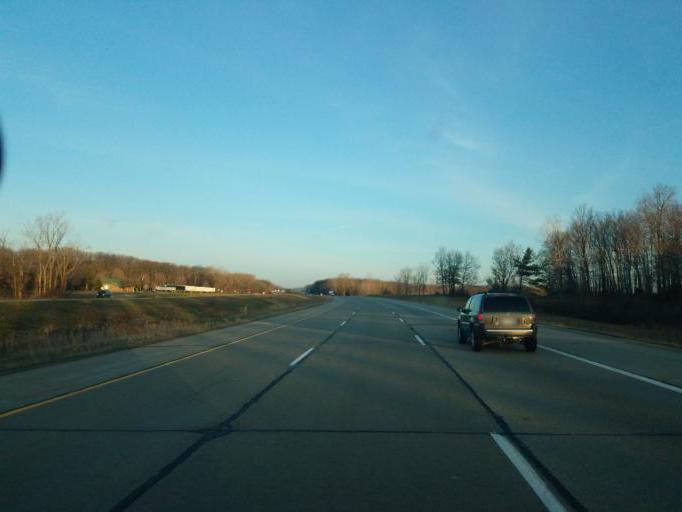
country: US
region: Michigan
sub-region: Livingston County
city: Howell
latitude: 42.6043
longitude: -83.9532
